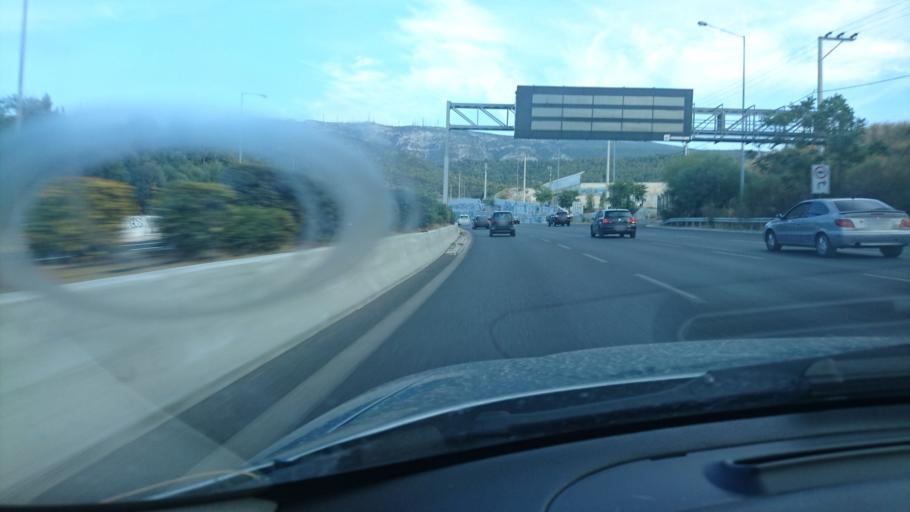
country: GR
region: Attica
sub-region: Nomos Attikis
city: Zografos
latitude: 37.9756
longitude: 23.7899
